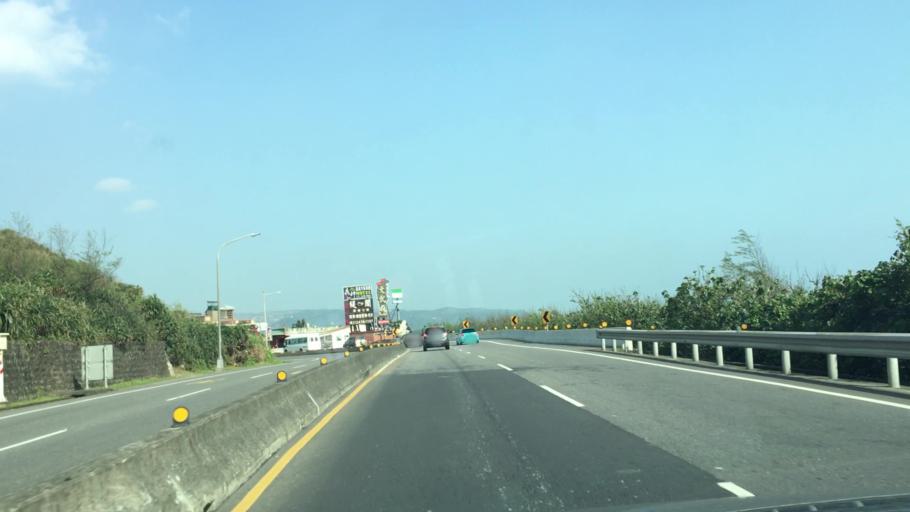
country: TW
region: Taiwan
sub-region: Keelung
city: Keelung
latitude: 25.2089
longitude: 121.6582
